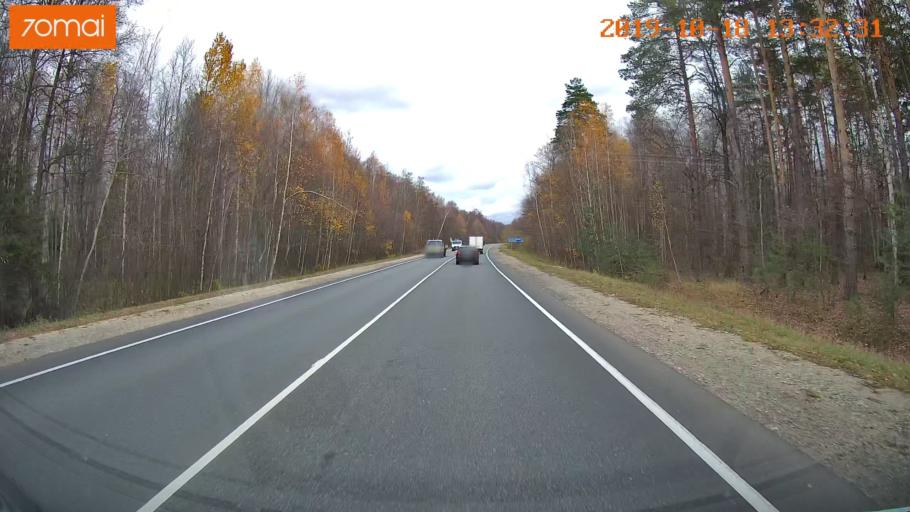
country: RU
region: Rjazan
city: Solotcha
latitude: 54.8342
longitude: 39.9196
